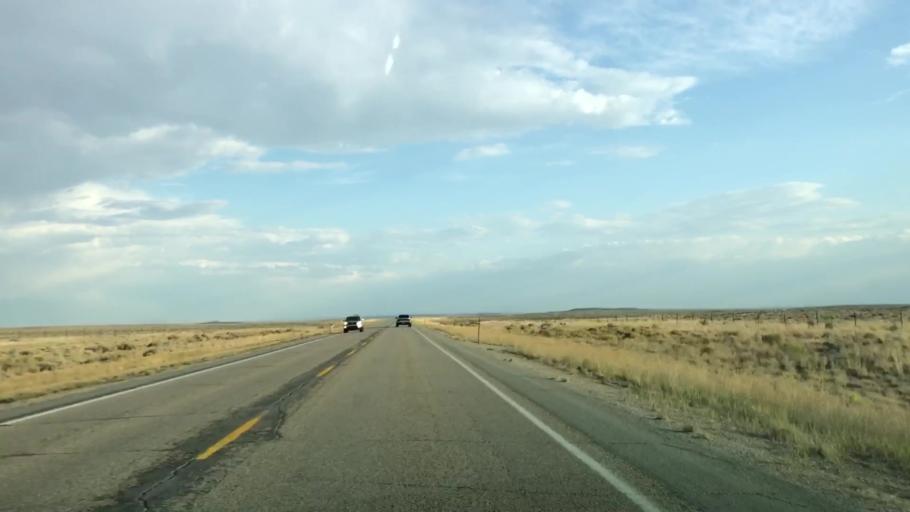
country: US
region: Wyoming
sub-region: Sublette County
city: Pinedale
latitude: 42.3986
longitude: -109.5451
